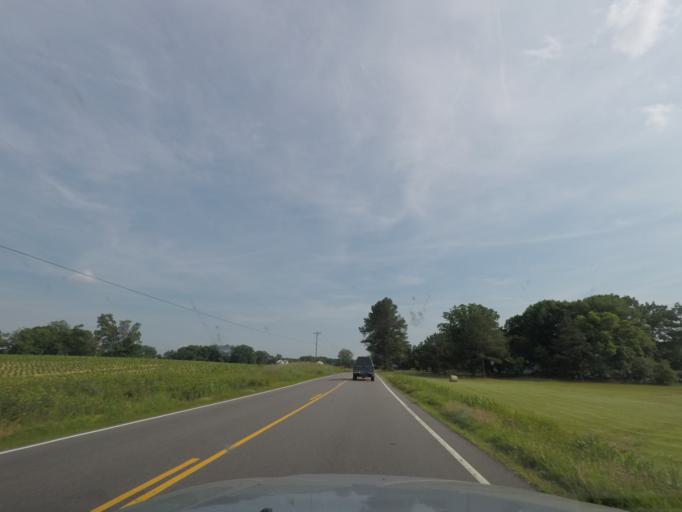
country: US
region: Virginia
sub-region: Mecklenburg County
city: Chase City
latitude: 36.8288
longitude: -78.5939
